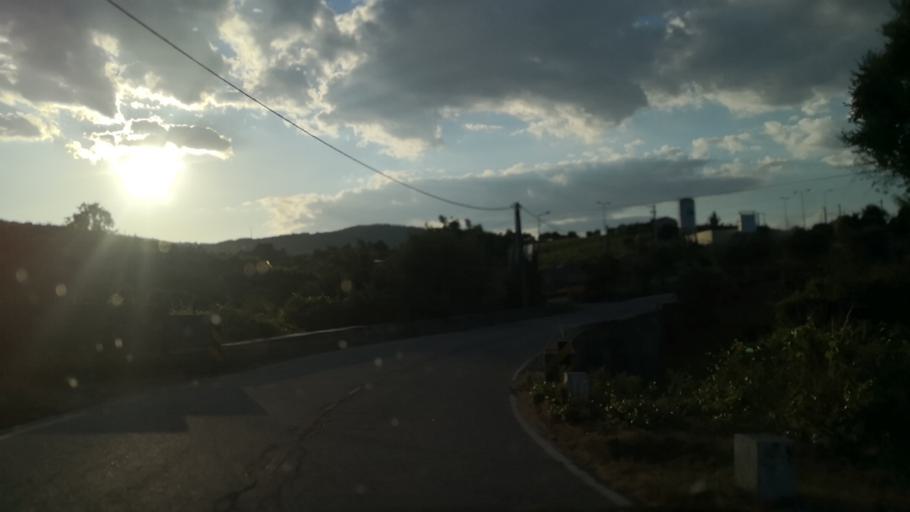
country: PT
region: Vila Real
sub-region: Sabrosa
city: Sabrosa
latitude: 41.2726
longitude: -7.4600
